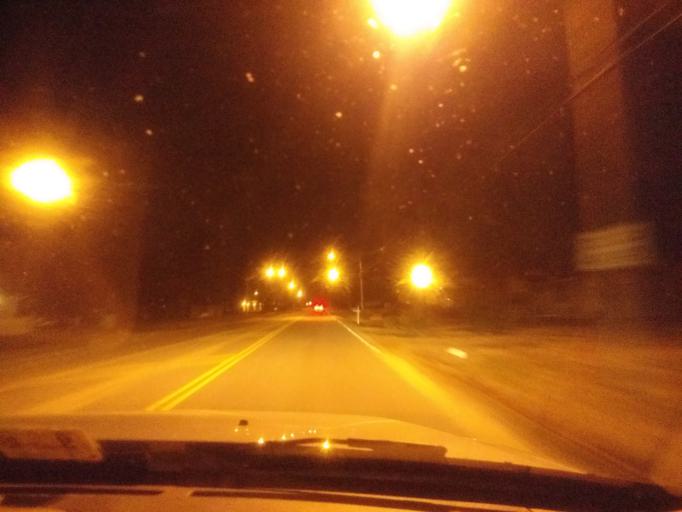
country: US
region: Virginia
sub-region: City of Chesapeake
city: Chesapeake
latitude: 36.7907
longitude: -76.1966
